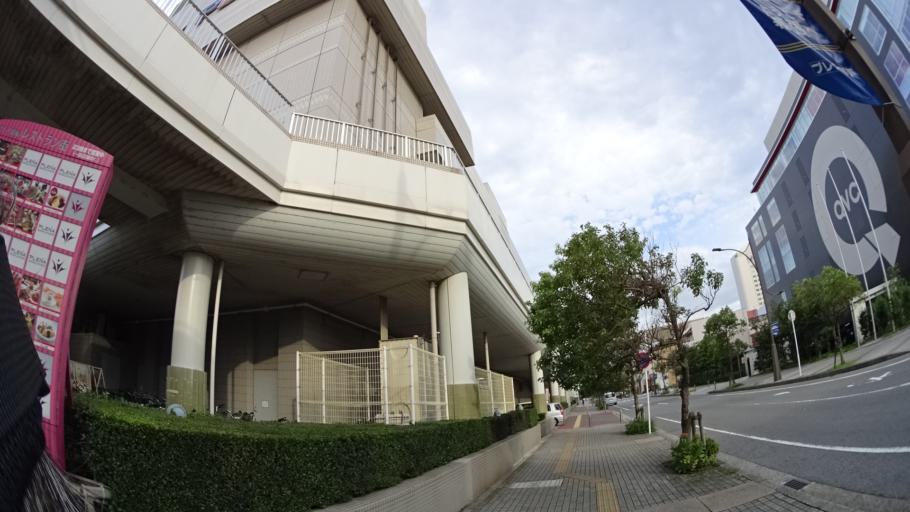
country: JP
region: Chiba
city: Funabashi
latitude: 35.6478
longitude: 140.0398
